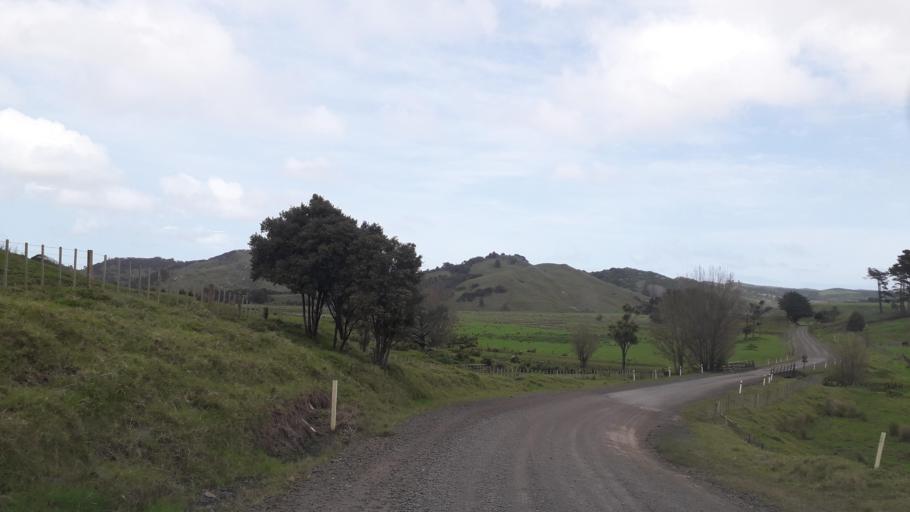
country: NZ
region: Northland
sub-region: Far North District
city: Kaitaia
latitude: -35.4159
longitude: 173.3646
